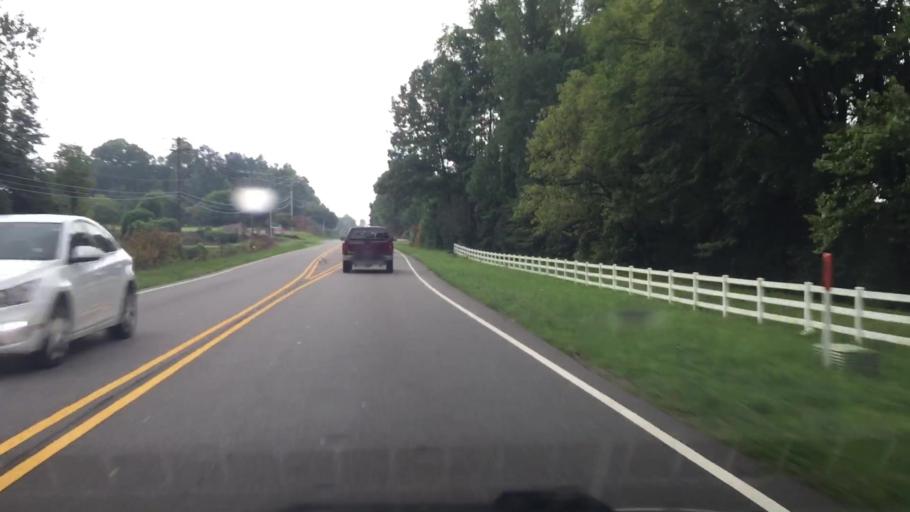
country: US
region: North Carolina
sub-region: Iredell County
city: Mooresville
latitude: 35.5663
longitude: -80.8473
